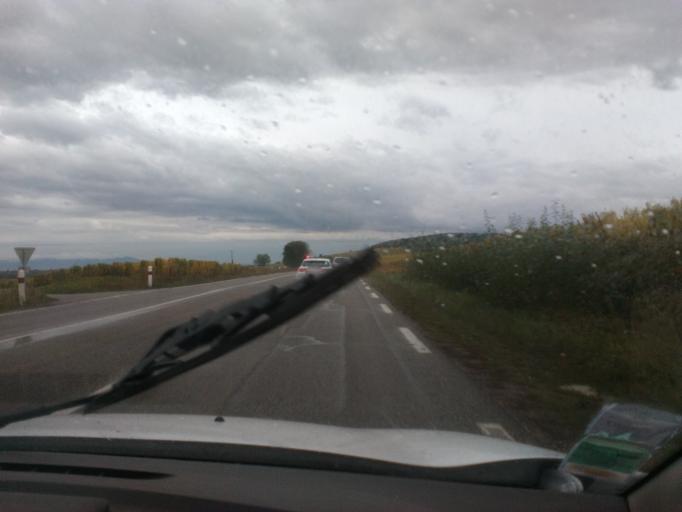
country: FR
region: Alsace
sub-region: Departement du Haut-Rhin
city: Ammerschwihr
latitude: 48.1183
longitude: 7.2885
